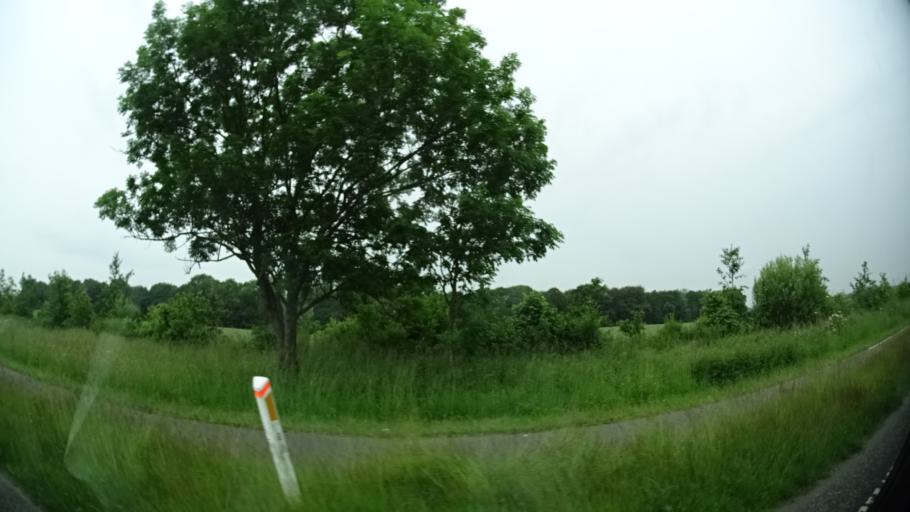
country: DK
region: Central Jutland
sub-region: Arhus Kommune
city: Hjortshoj
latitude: 56.2392
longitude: 10.2984
